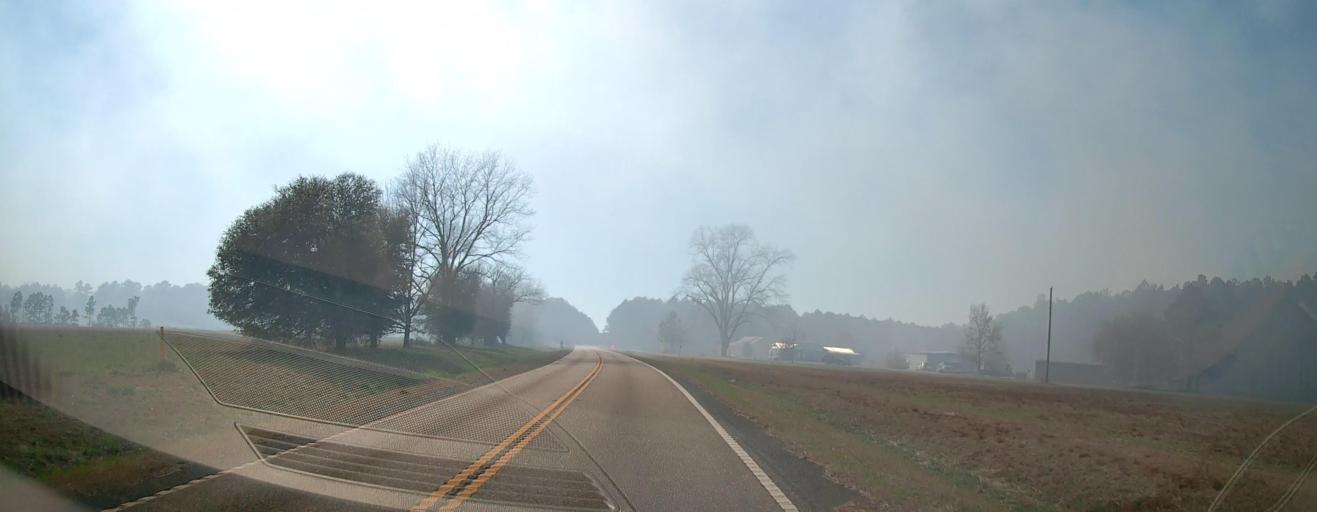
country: US
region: Georgia
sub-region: Schley County
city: Ellaville
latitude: 32.1922
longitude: -84.2224
